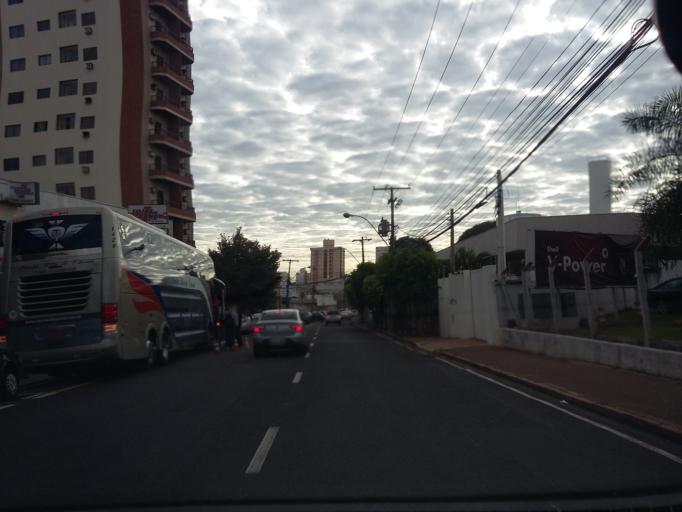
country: BR
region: Sao Paulo
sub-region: Sao Jose Do Rio Preto
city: Sao Jose do Rio Preto
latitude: -20.8226
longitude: -49.3924
